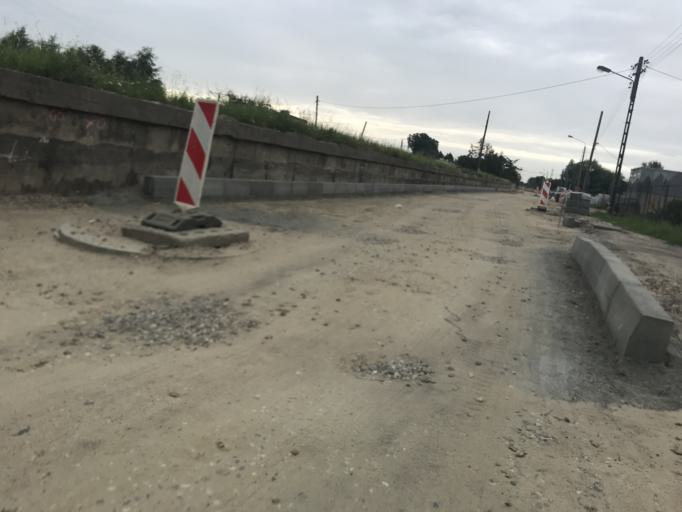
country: PL
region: Pomeranian Voivodeship
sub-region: Gdansk
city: Gdansk
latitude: 54.3420
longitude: 18.6841
